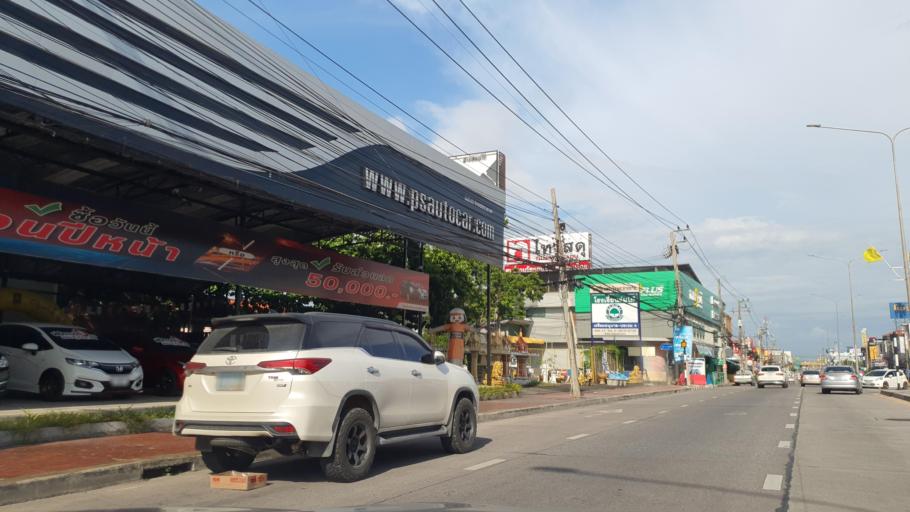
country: TH
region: Chon Buri
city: Chon Buri
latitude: 13.3572
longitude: 100.9962
